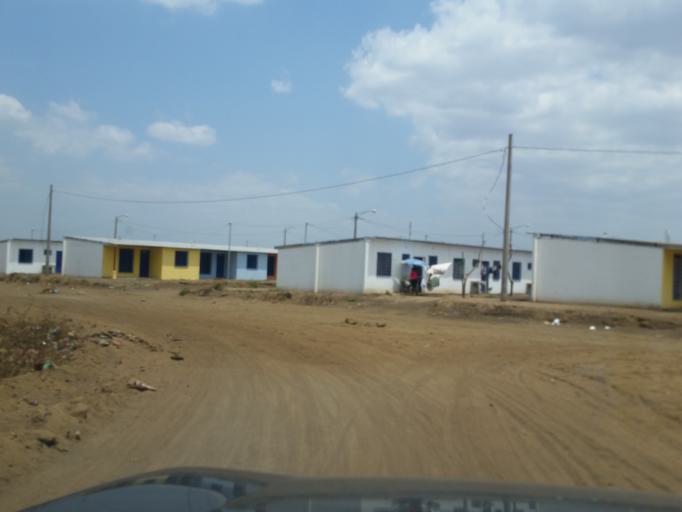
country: NI
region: Managua
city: Managua
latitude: 12.1334
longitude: -86.1616
